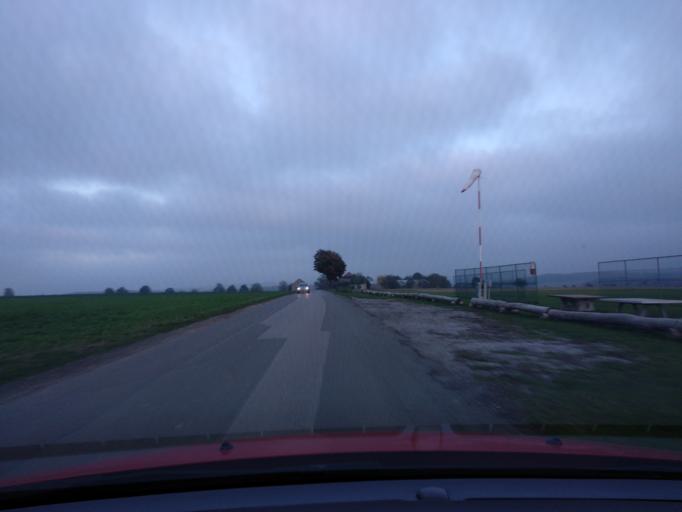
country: DE
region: North Rhine-Westphalia
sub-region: Regierungsbezirk Detmold
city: Paderborn
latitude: 51.6762
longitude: 8.7626
